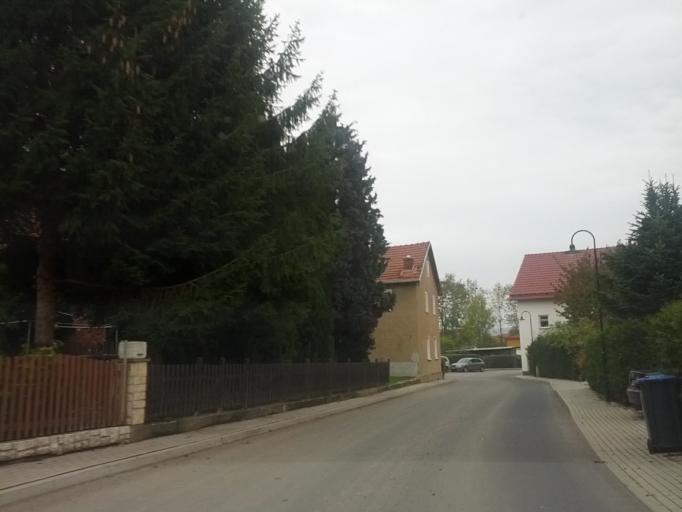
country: DE
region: Thuringia
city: Creuzburg
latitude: 51.0222
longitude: 10.2250
